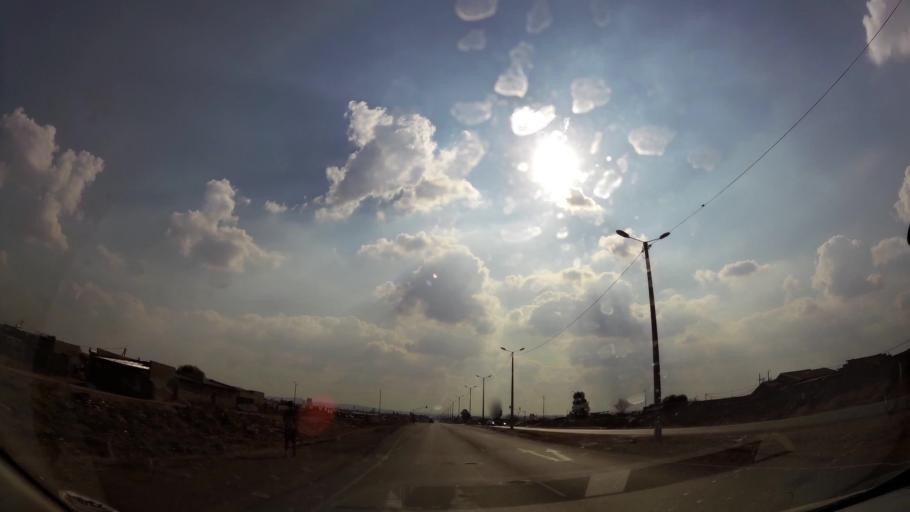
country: ZA
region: Gauteng
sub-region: Ekurhuleni Metropolitan Municipality
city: Germiston
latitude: -26.3165
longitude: 28.2097
